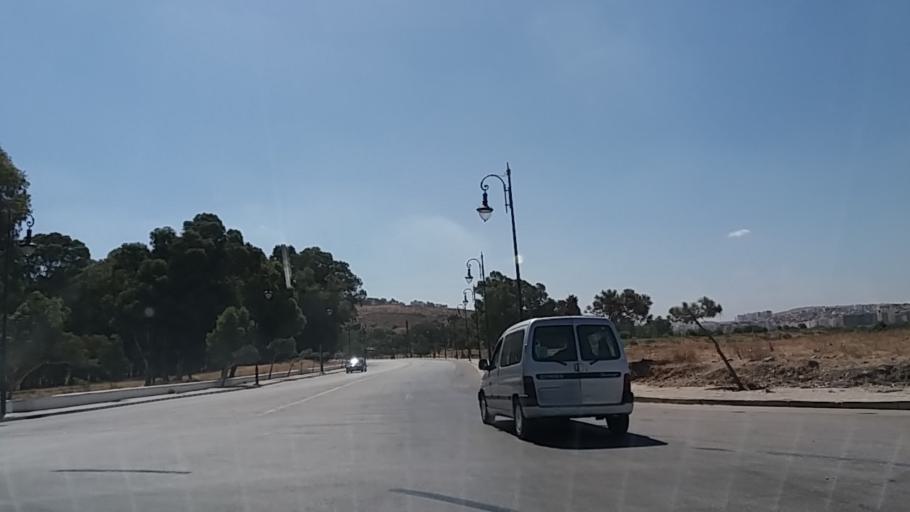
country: MA
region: Tanger-Tetouan
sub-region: Tanger-Assilah
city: Tangier
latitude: 35.7798
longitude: -5.7653
